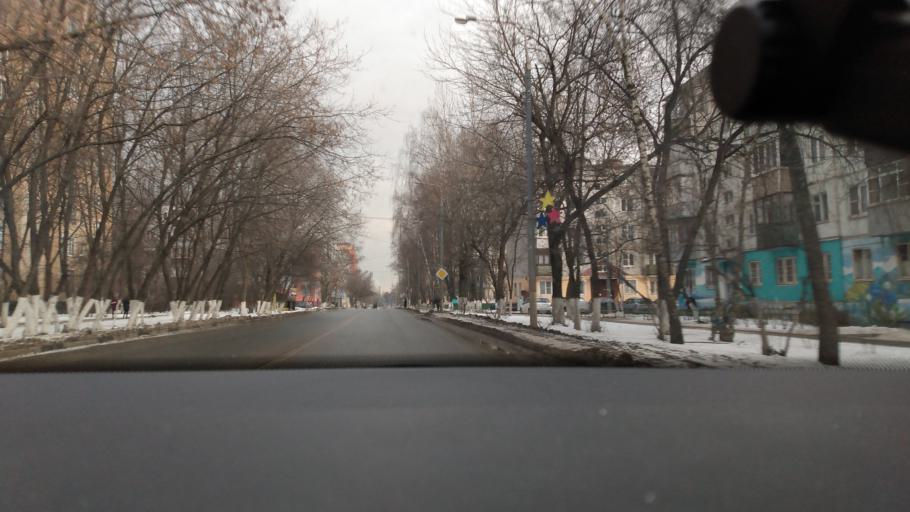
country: RU
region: Moskovskaya
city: Zheleznodorozhnyy
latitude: 55.7433
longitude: 38.0268
